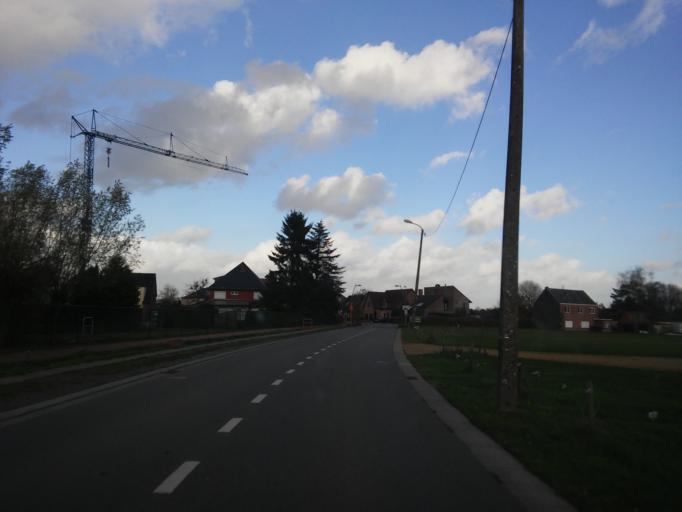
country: BE
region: Flanders
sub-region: Provincie Antwerpen
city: Puurs
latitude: 51.0692
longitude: 4.2821
